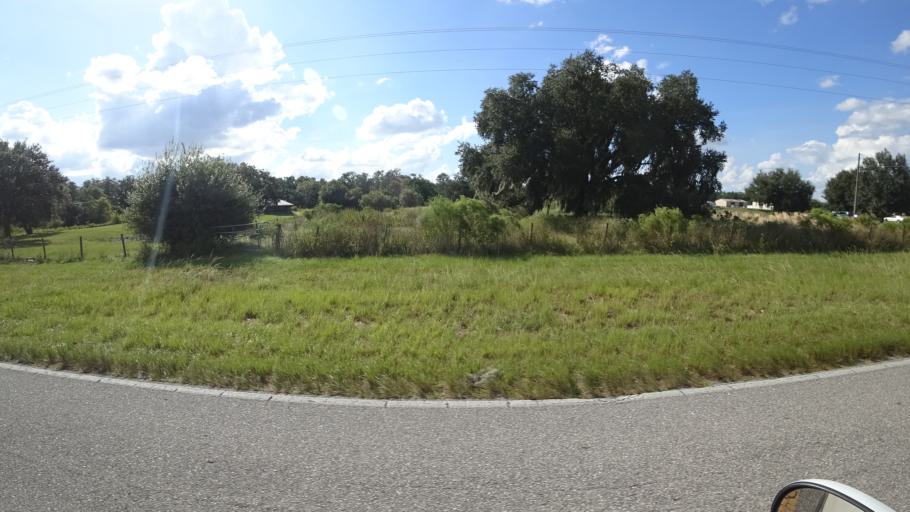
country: US
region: Florida
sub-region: DeSoto County
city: Nocatee
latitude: 27.2889
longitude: -82.1134
